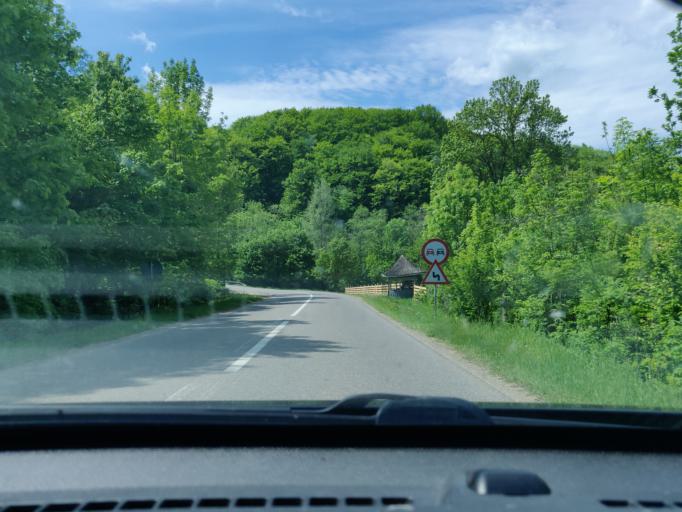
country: RO
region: Vrancea
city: Dragosloveni
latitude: 46.0293
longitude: 26.6908
